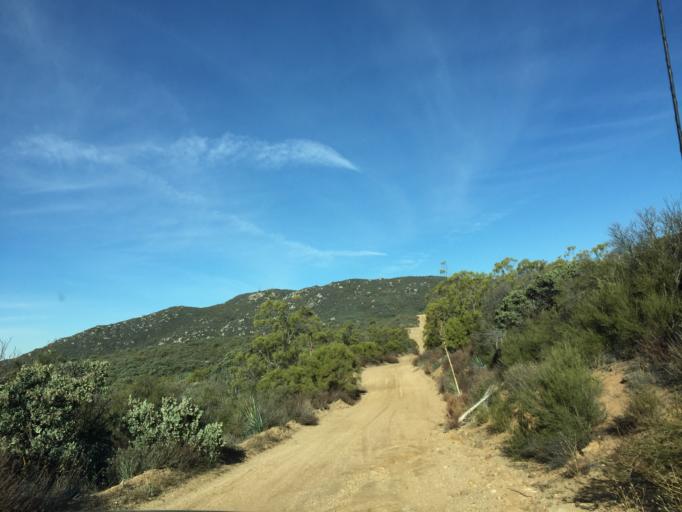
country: US
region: California
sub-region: Riverside County
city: Valle Vista
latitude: 33.6248
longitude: -116.8229
